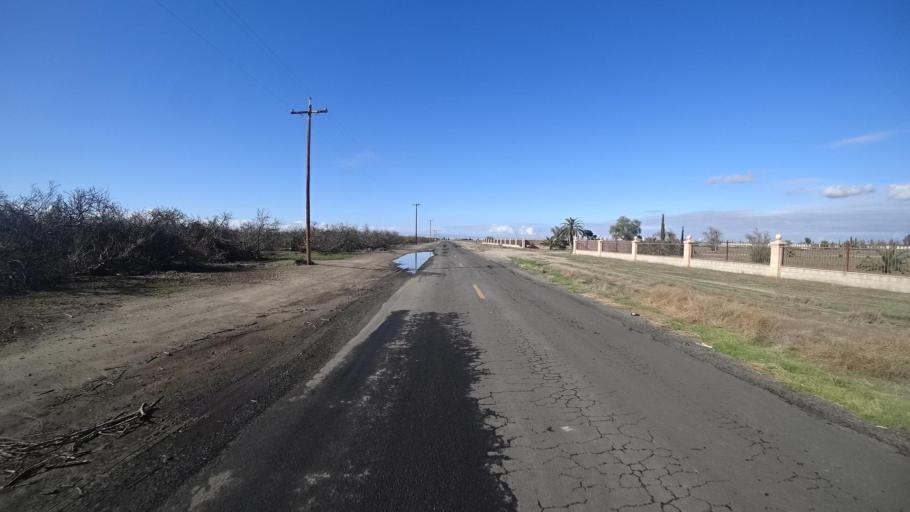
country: US
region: California
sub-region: Kern County
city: Rosedale
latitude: 35.3689
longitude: -119.2285
